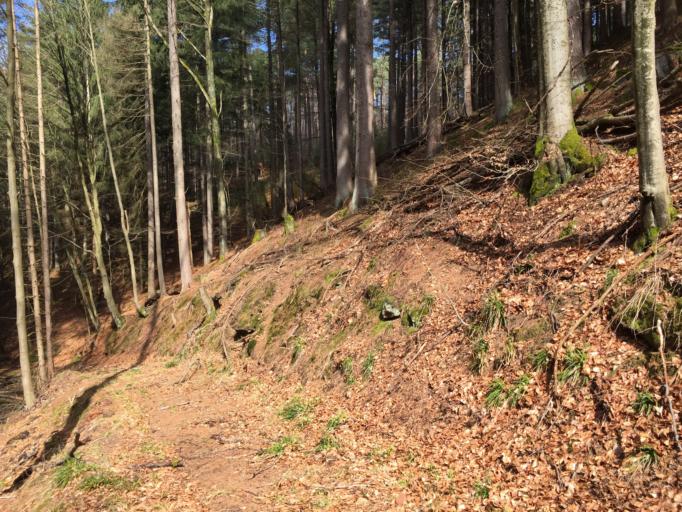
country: DE
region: Rheinland-Pfalz
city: Elmstein
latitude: 49.3912
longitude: 7.9425
